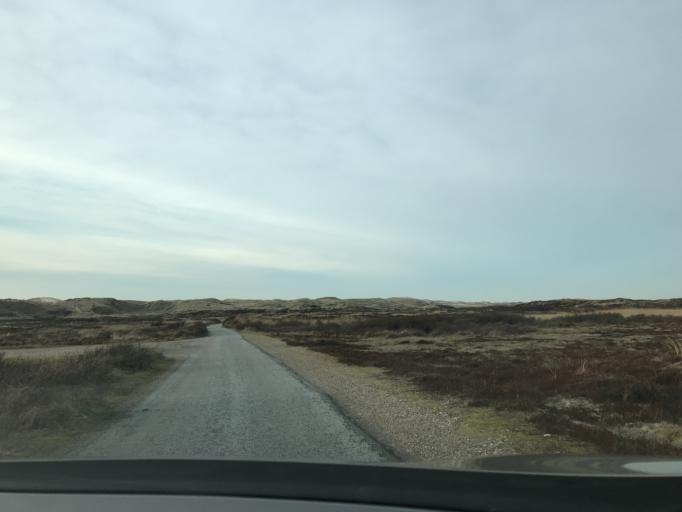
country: DK
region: Central Jutland
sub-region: Ringkobing-Skjern Kommune
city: Hvide Sande
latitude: 55.8081
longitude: 8.1809
